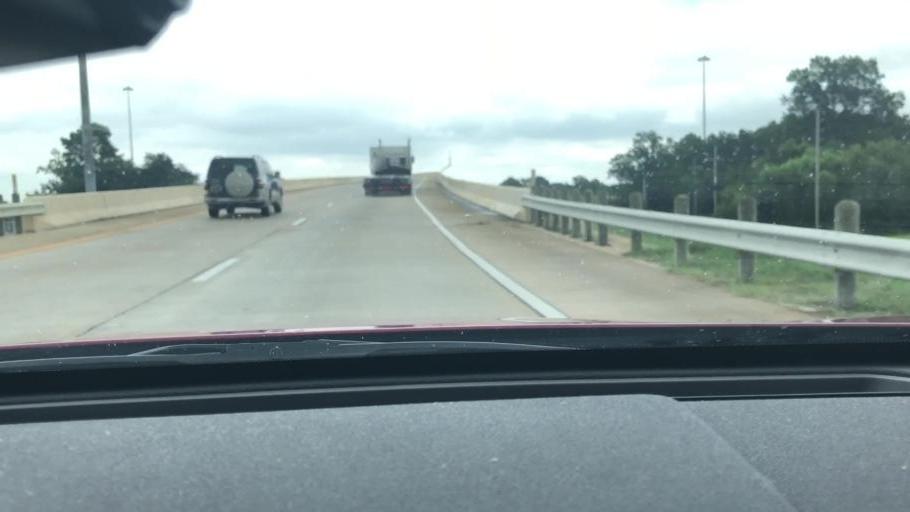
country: US
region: Texas
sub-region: Bowie County
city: Wake Village
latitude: 33.3924
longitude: -94.1014
